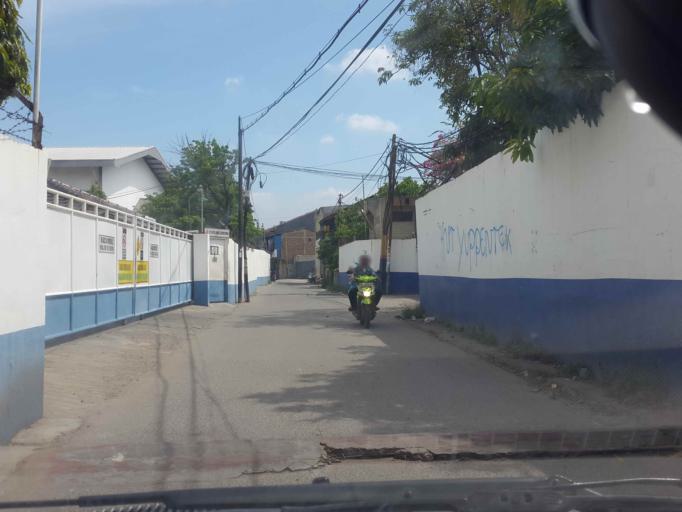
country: ID
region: Banten
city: Tangerang
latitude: -6.1517
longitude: 106.6810
